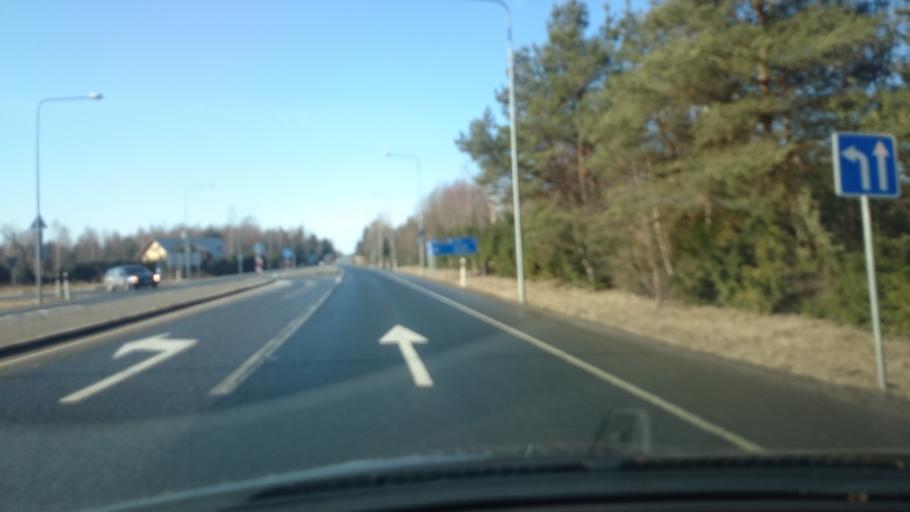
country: EE
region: Raplamaa
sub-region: Rapla vald
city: Rapla
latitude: 59.0403
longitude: 24.8371
